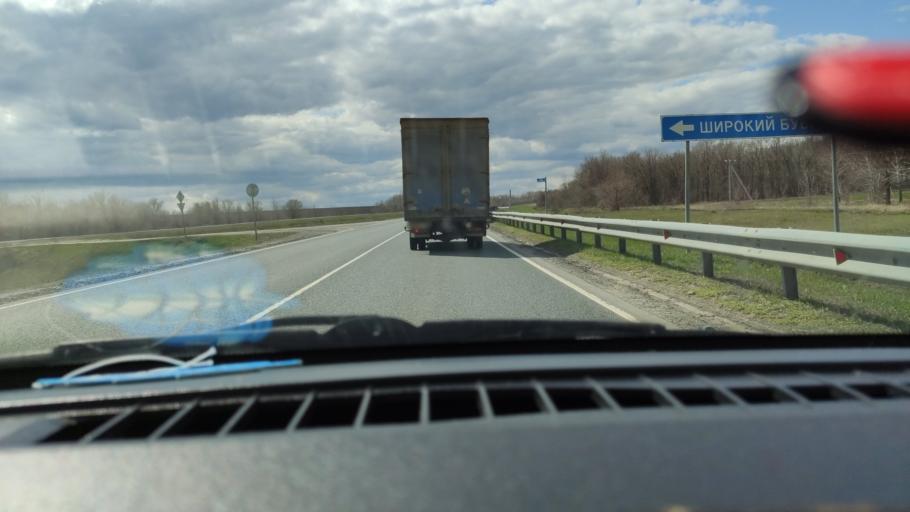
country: RU
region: Saratov
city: Balakovo
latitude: 52.1065
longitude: 47.7437
